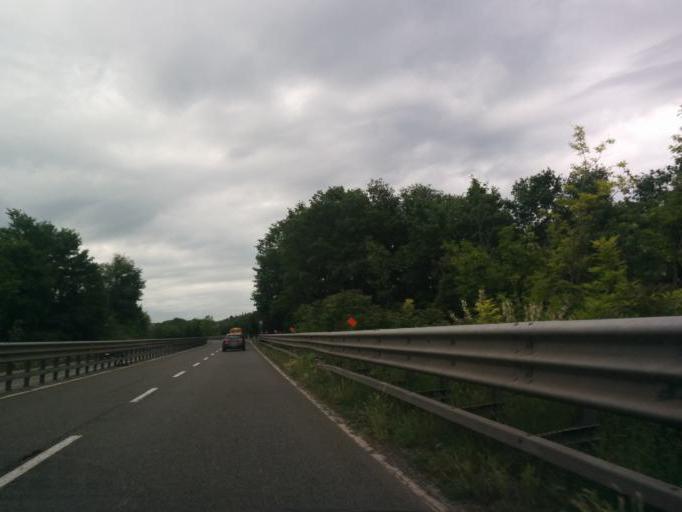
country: IT
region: Tuscany
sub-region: Provincia di Siena
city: Monteriggioni
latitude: 43.3916
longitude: 11.2461
